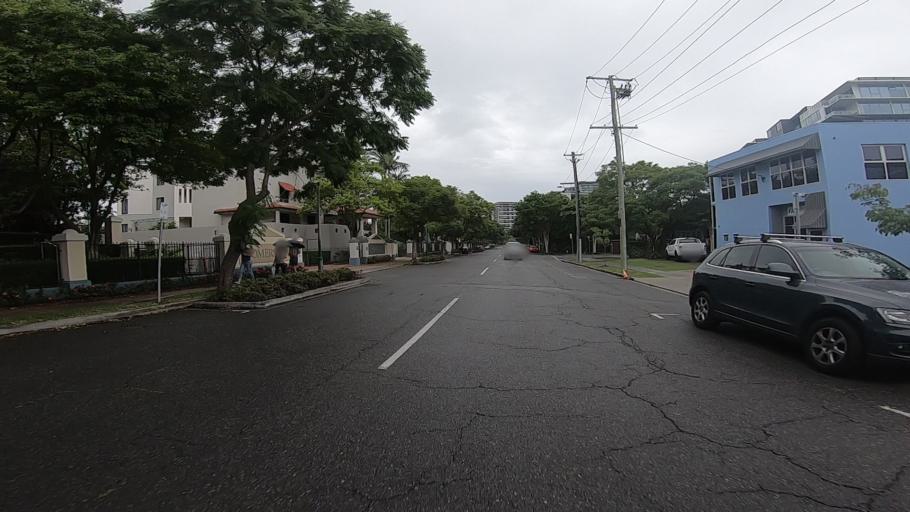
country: AU
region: Queensland
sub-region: Brisbane
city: Fortitude Valley
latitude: -27.4459
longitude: 153.0456
